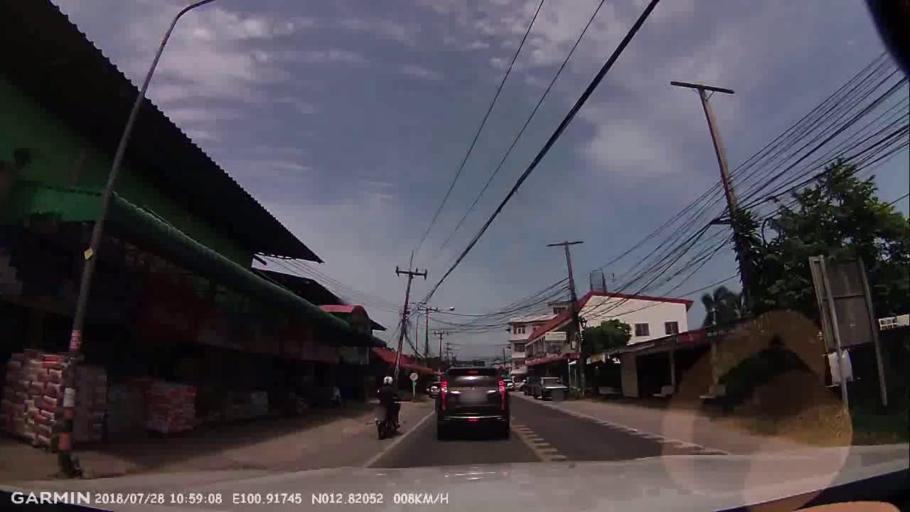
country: TH
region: Chon Buri
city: Phatthaya
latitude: 12.8205
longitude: 100.9174
